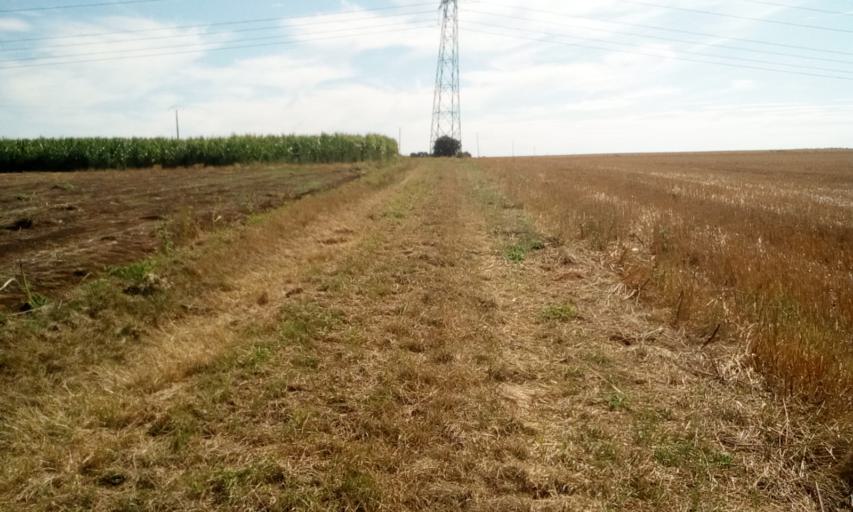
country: FR
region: Lower Normandy
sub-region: Departement du Calvados
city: Eterville
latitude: 49.1208
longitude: -0.4312
